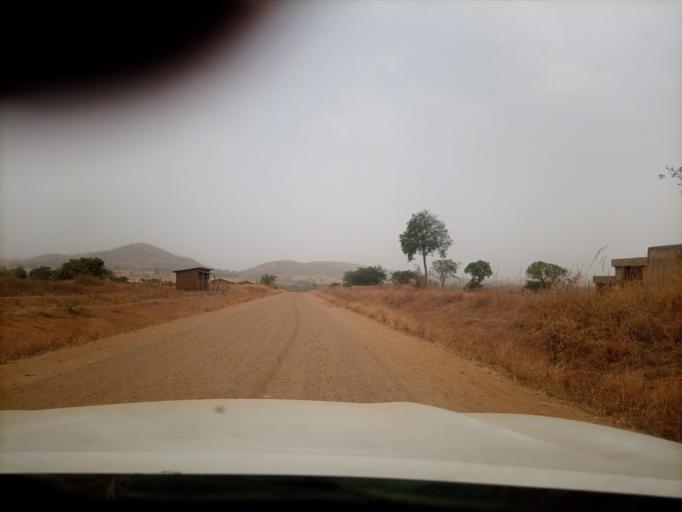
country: ET
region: Oromiya
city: Mendi
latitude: 10.2018
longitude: 35.0900
